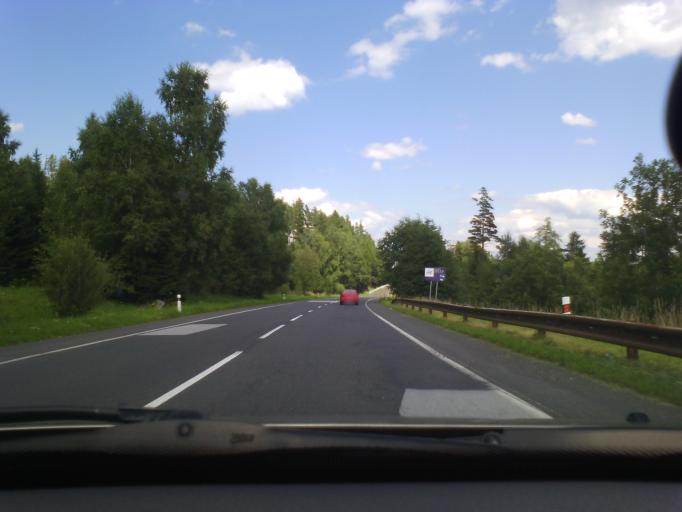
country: SK
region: Presovsky
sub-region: Okres Poprad
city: Vysoke Tatry
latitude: 49.1532
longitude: 20.2660
